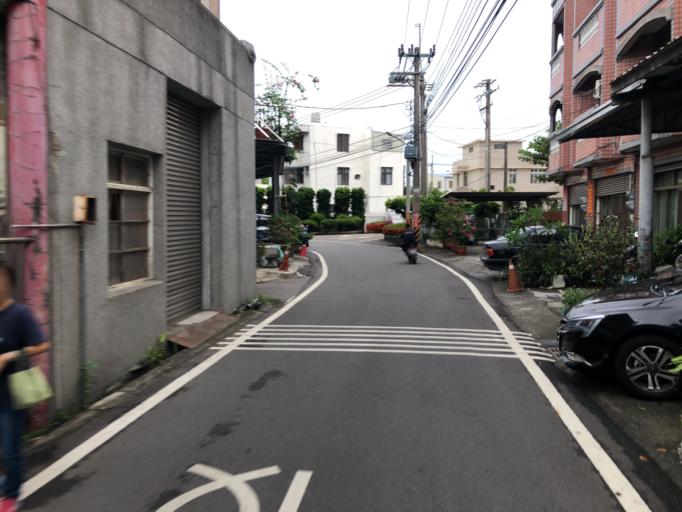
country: TW
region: Taiwan
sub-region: Taichung City
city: Taichung
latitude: 24.0622
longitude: 120.6816
